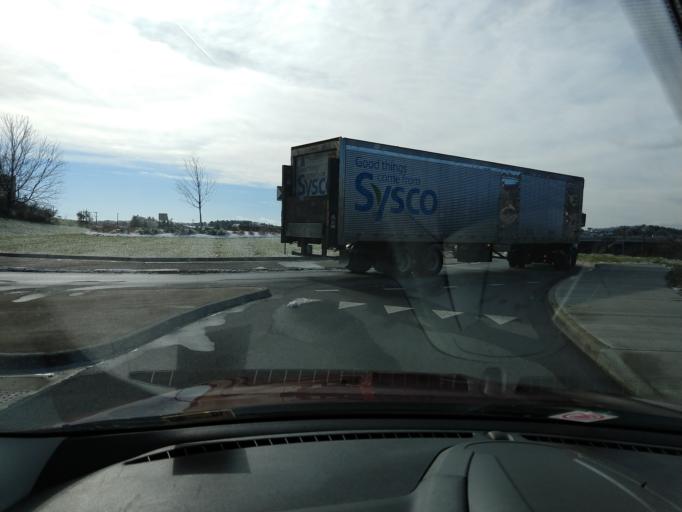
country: US
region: Virginia
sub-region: City of Staunton
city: Staunton
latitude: 38.1330
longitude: -79.0381
